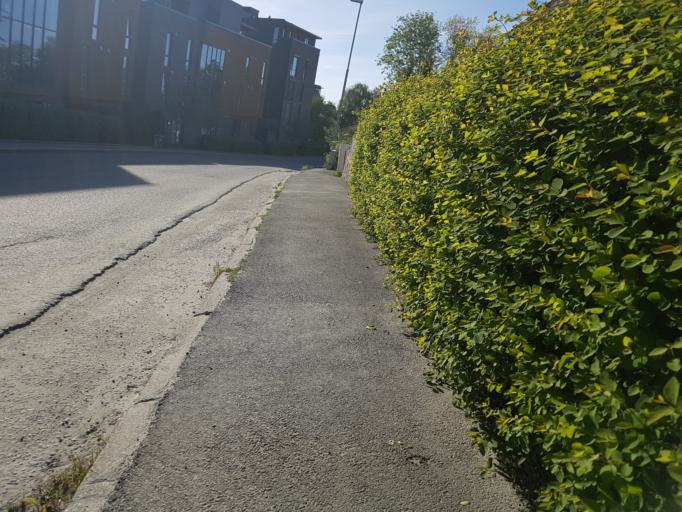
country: NO
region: Sor-Trondelag
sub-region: Trondheim
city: Trondheim
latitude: 63.4314
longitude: 10.4249
